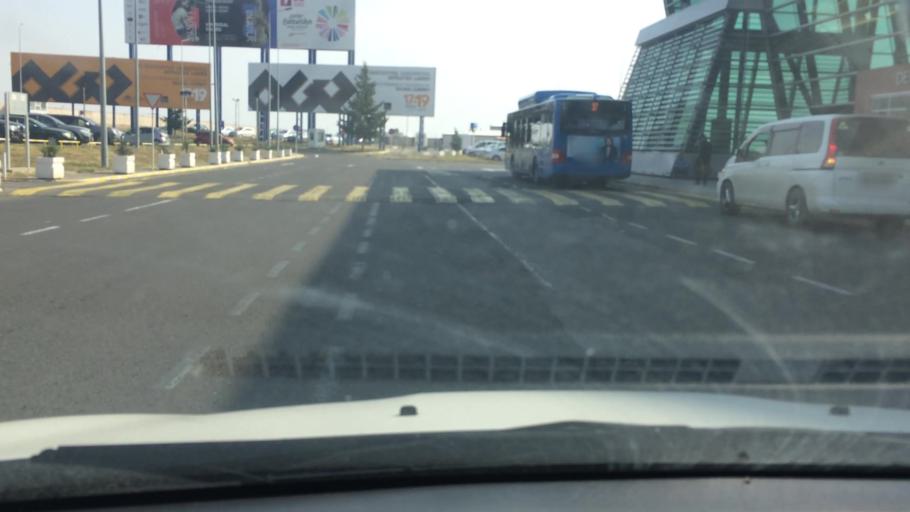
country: GE
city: Didi Lilo
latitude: 41.6698
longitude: 44.9652
